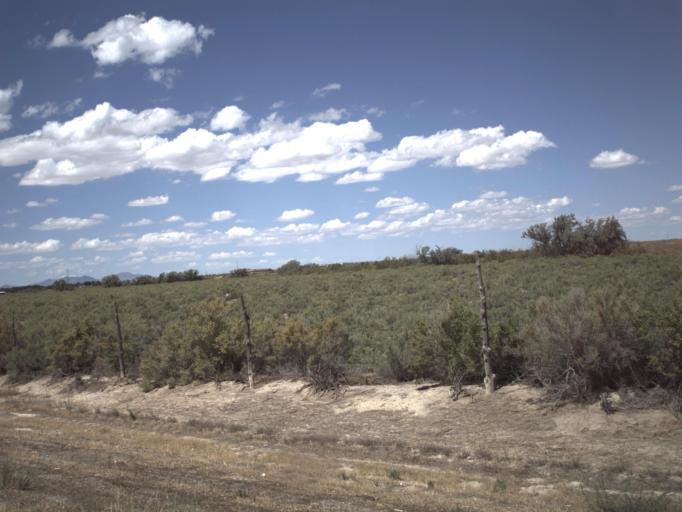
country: US
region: Utah
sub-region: Millard County
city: Delta
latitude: 39.3530
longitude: -112.5310
